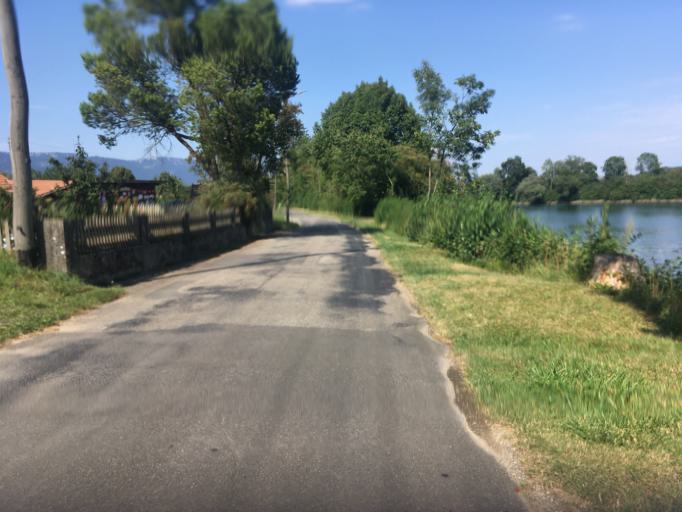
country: CH
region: Bern
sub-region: Biel/Bienne District
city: Meinisberg
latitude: 47.1462
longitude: 7.3833
